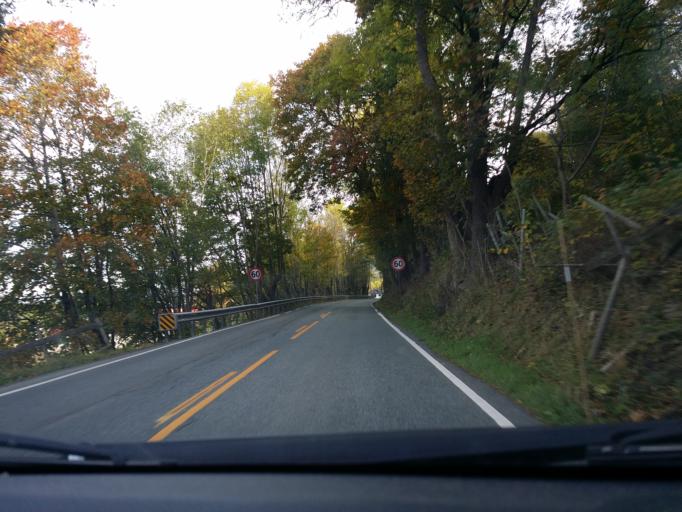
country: NO
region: Buskerud
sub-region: Lier
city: Tranby
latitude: 59.8721
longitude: 10.2919
